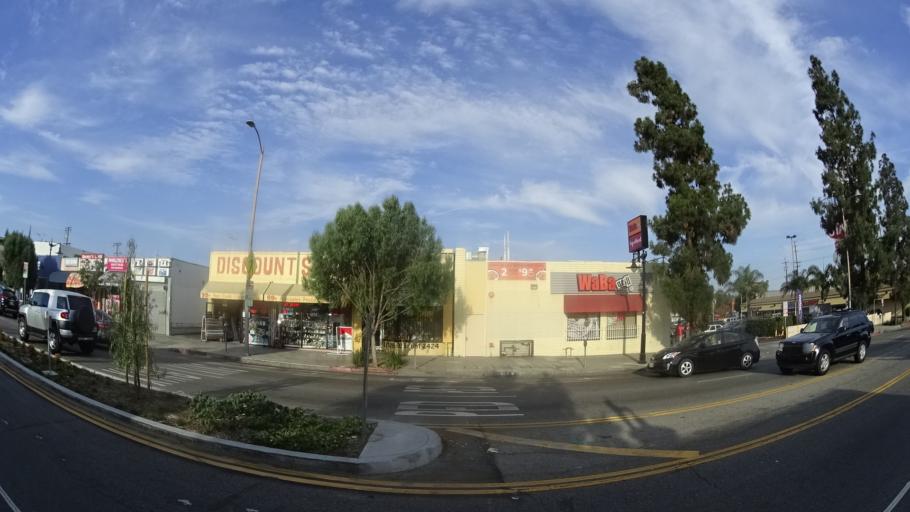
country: US
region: California
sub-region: Los Angeles County
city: Silver Lake
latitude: 34.0920
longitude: -118.2919
